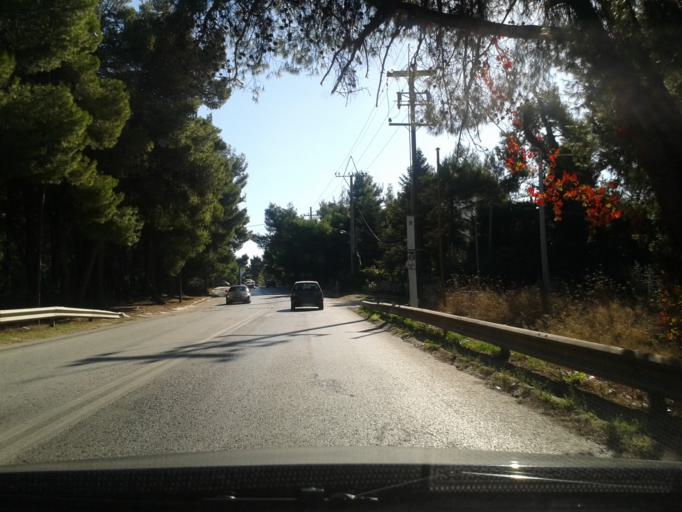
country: GR
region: Attica
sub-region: Nomarchia Anatolikis Attikis
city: Dionysos
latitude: 38.1051
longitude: 23.8690
